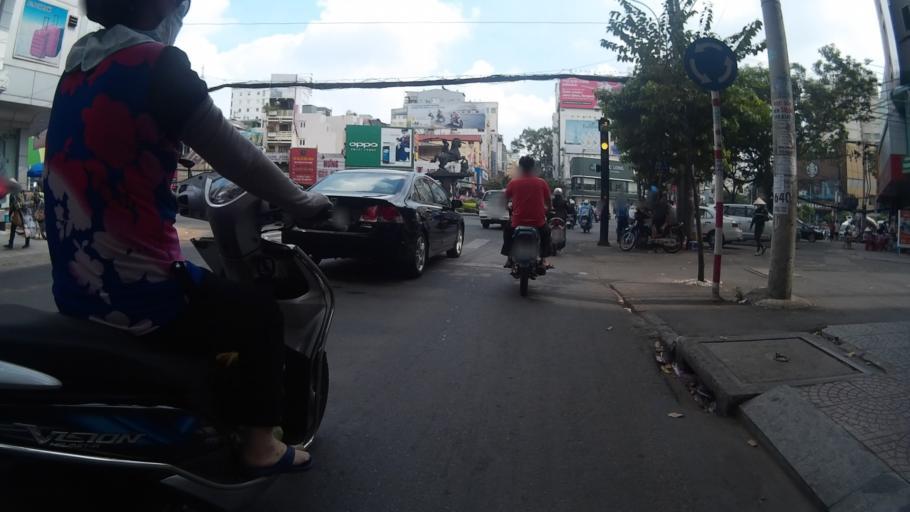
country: VN
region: Ho Chi Minh City
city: Quan Ba
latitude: 10.7710
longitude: 106.6928
